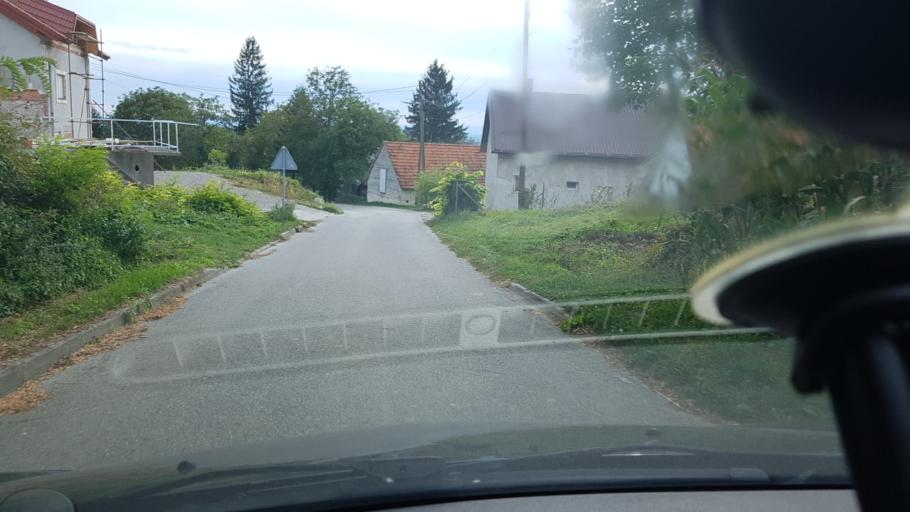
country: HR
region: Krapinsko-Zagorska
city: Radoboj
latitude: 46.1742
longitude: 15.9492
